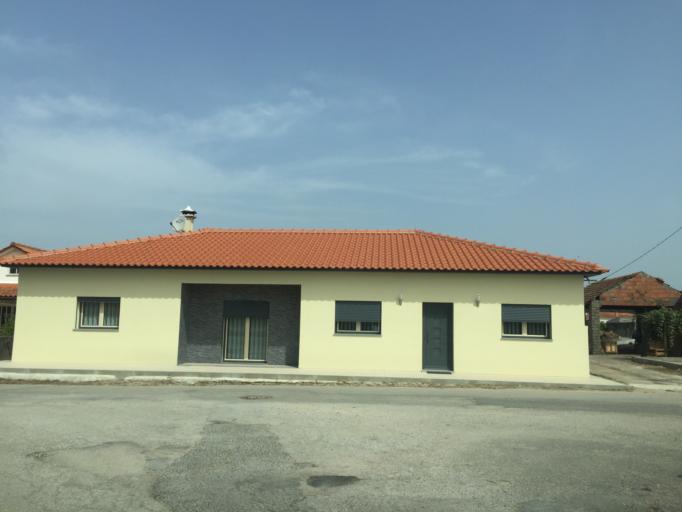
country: PT
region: Leiria
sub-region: Pombal
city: Lourical
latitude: 39.9681
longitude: -8.7962
